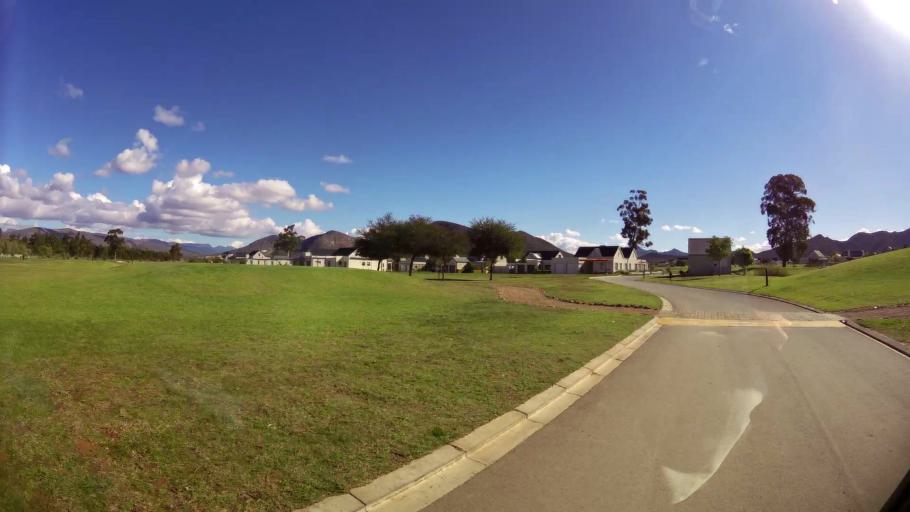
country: ZA
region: Western Cape
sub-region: Cape Winelands District Municipality
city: Ashton
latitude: -33.8141
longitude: 19.8493
